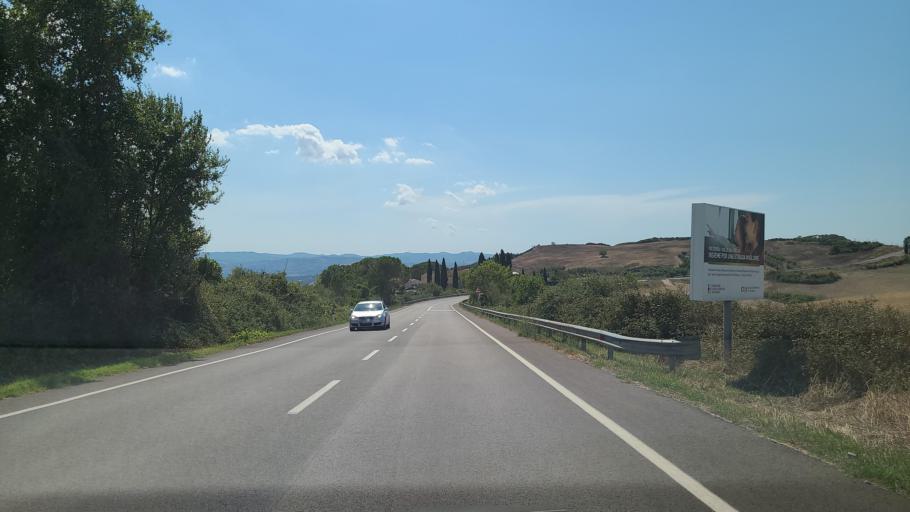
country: IT
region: Tuscany
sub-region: Province of Pisa
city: Volterra
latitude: 43.3847
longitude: 10.9381
